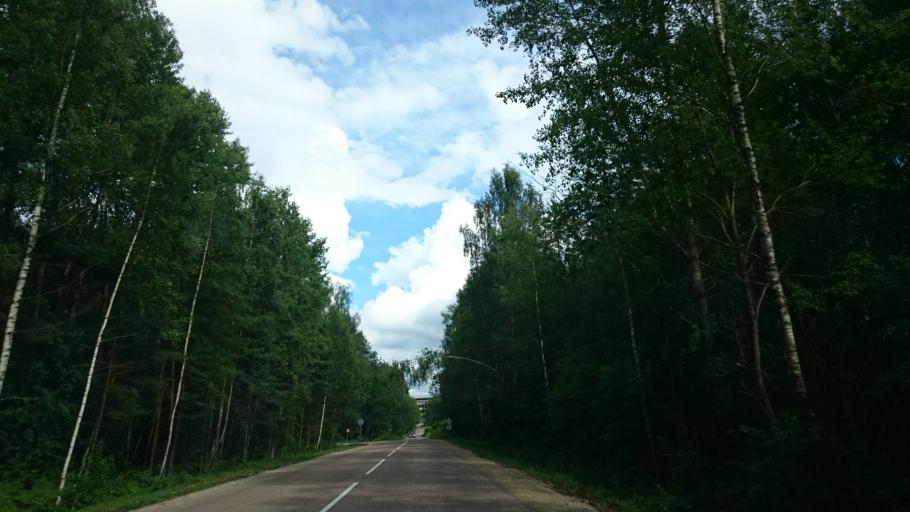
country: LV
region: Salaspils
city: Salaspils
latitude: 56.8683
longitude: 24.3889
